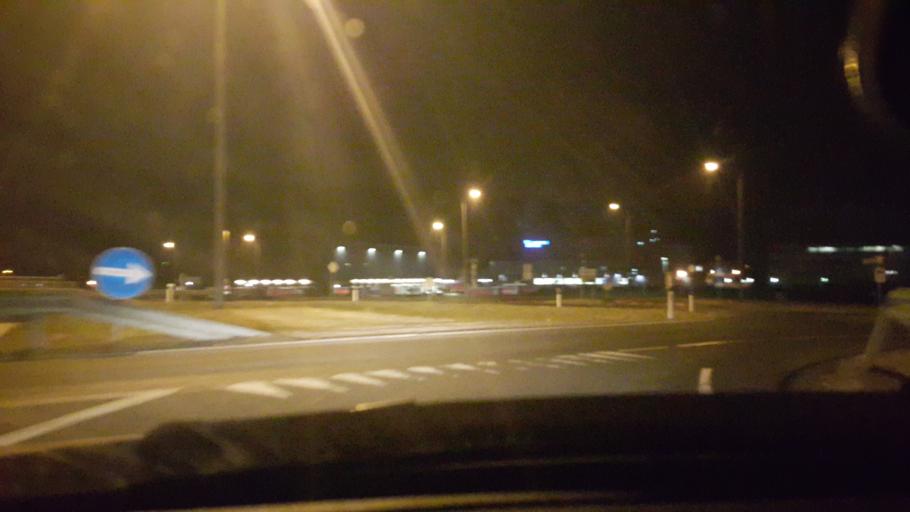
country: AT
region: Styria
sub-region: Politischer Bezirk Graz-Umgebung
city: Feldkirchen bei Graz
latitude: 47.0304
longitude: 15.4260
